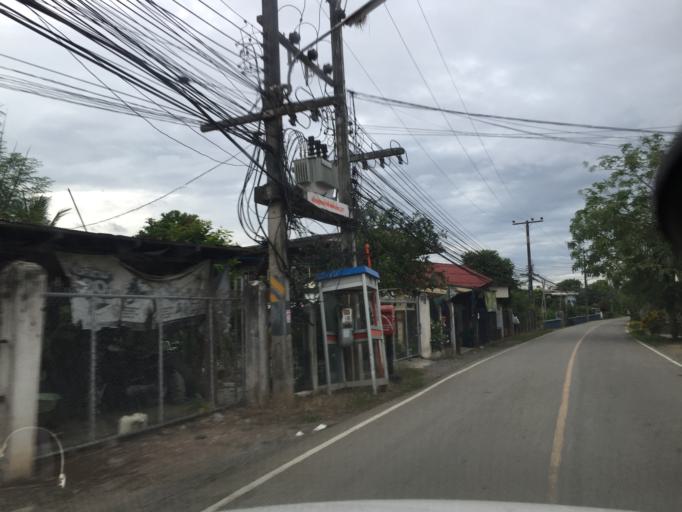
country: TH
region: Chiang Mai
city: Mae On
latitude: 18.8298
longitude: 99.1846
